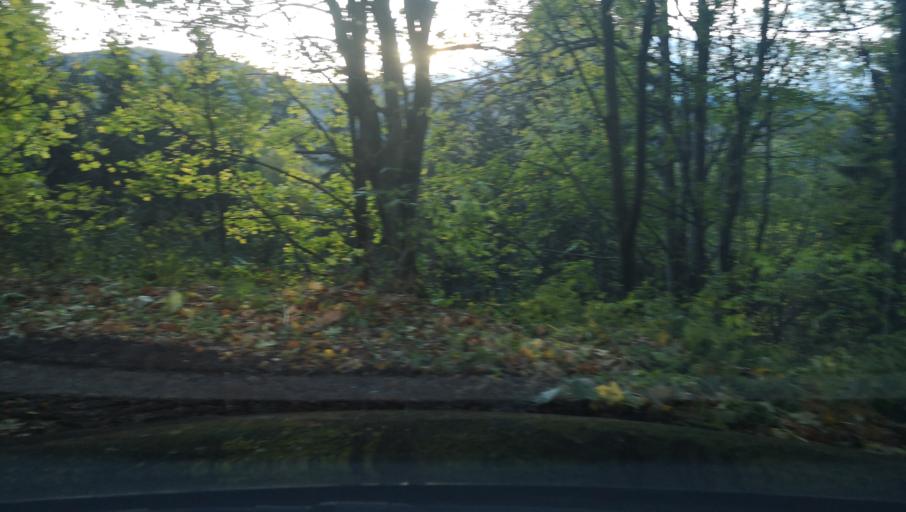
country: AT
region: Styria
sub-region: Politischer Bezirk Weiz
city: Birkfeld
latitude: 47.3355
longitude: 15.6392
